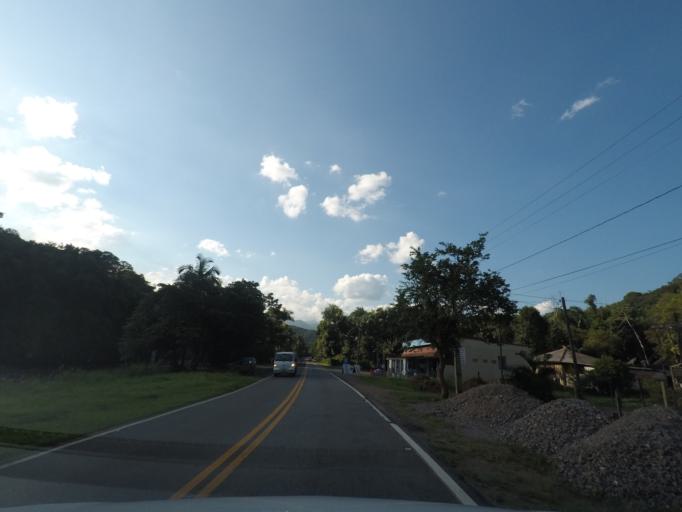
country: BR
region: Parana
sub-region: Antonina
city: Antonina
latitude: -25.4033
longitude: -48.8726
